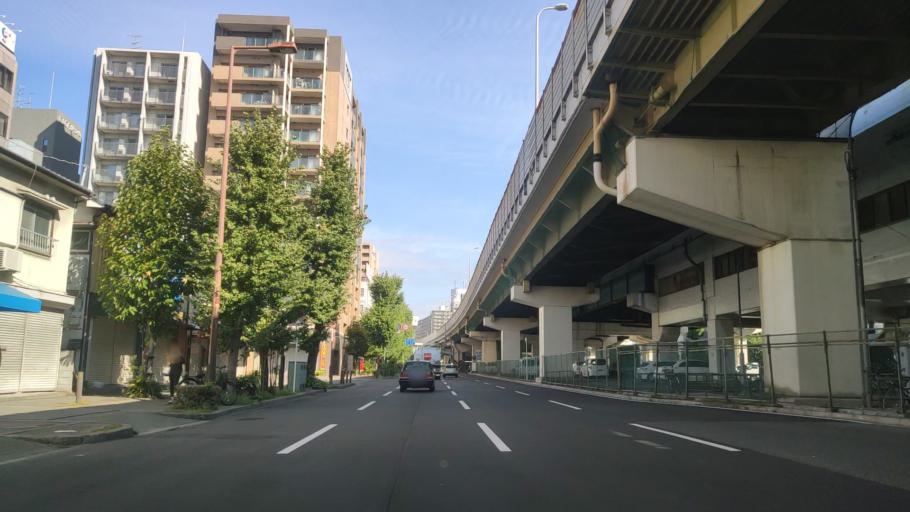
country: JP
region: Osaka
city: Suita
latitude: 34.7401
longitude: 135.4984
